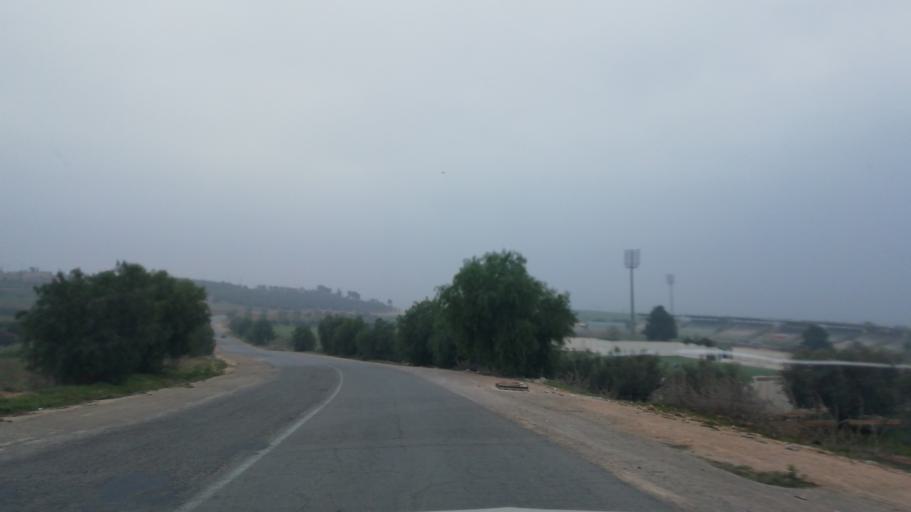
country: DZ
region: Mascara
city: Mascara
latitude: 35.3912
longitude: 0.1607
